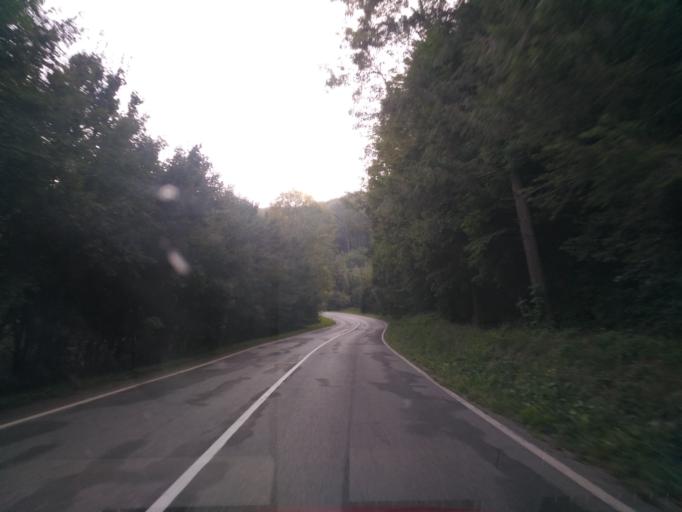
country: SK
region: Presovsky
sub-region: Okres Presov
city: Presov
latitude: 48.9895
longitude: 21.1897
